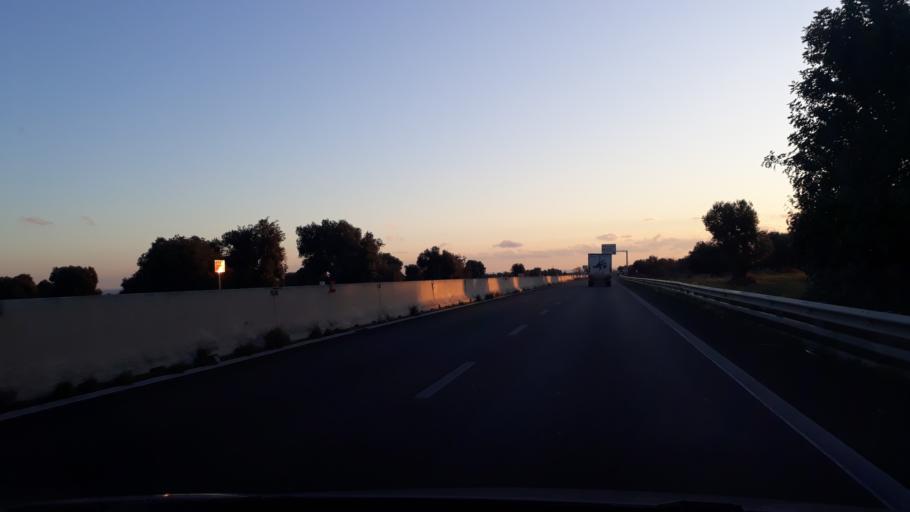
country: IT
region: Apulia
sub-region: Provincia di Brindisi
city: Pezze di Greco
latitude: 40.8339
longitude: 17.4025
